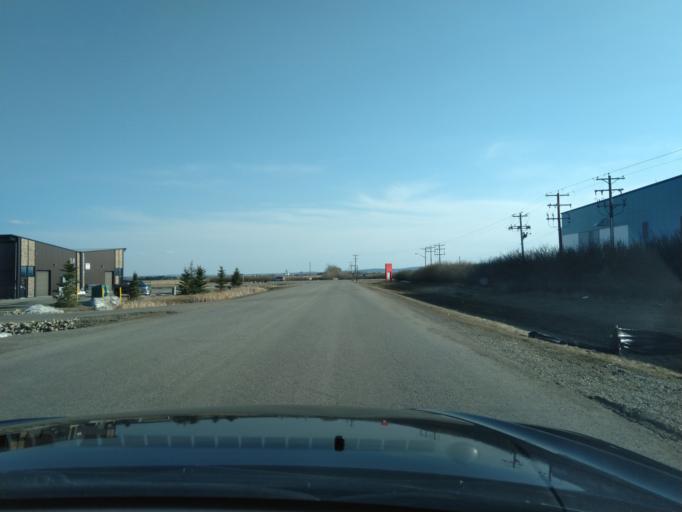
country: CA
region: Alberta
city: Cochrane
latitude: 51.0980
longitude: -114.3738
